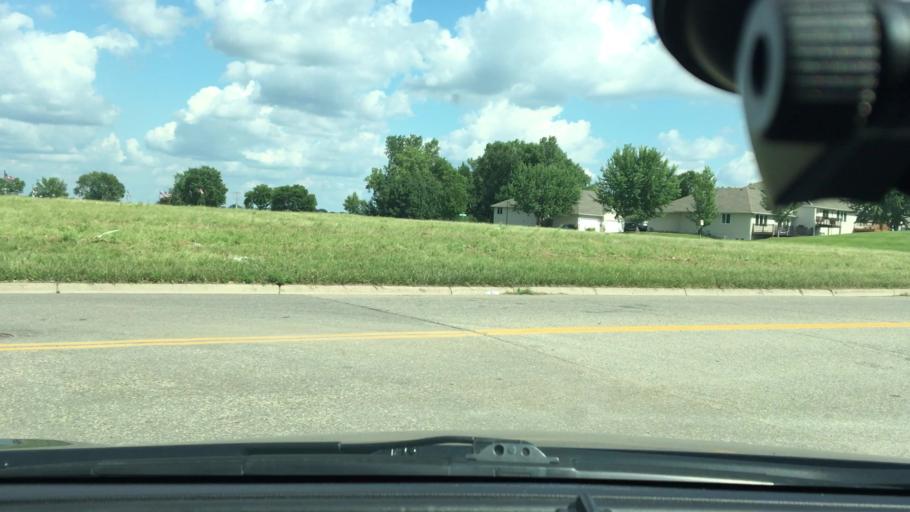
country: US
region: Minnesota
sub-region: Hennepin County
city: New Hope
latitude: 45.0560
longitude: -93.4081
